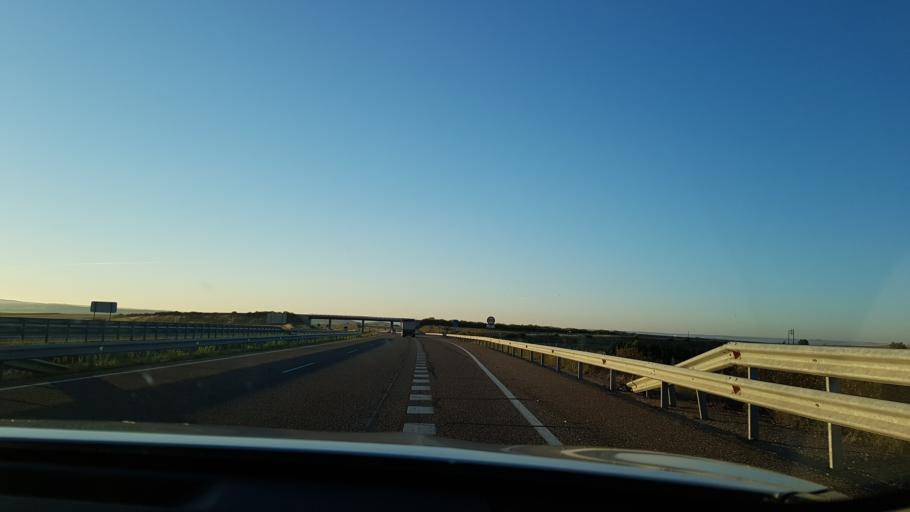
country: ES
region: Castille and Leon
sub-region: Provincia de Zamora
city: Valcabado
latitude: 41.5584
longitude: -5.7547
